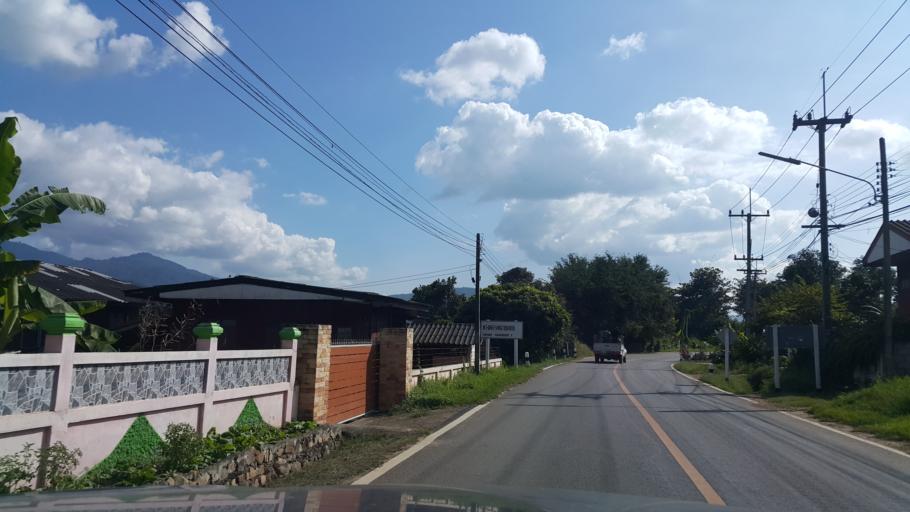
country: TH
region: Lamphun
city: Mae Tha
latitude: 18.5600
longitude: 99.2570
